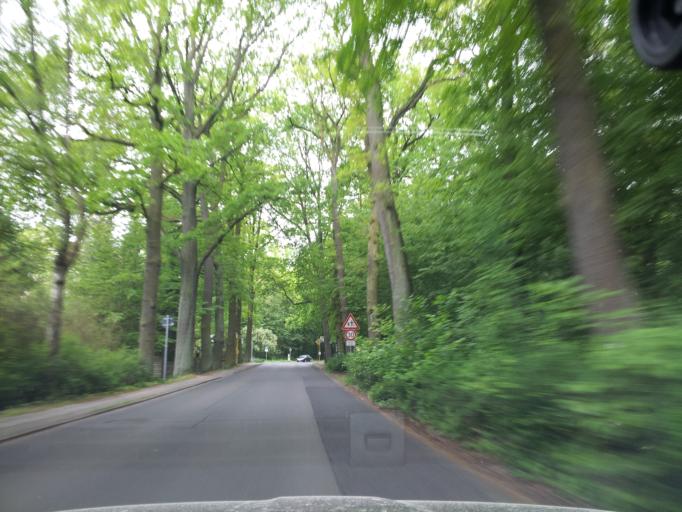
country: DE
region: Brandenburg
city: Dallgow-Doeberitz
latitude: 52.5773
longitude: 13.0616
